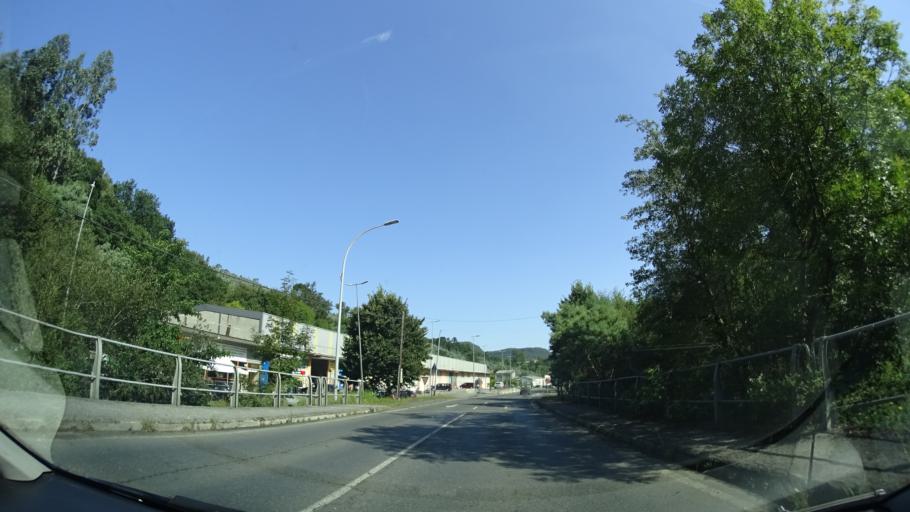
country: ES
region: Basque Country
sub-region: Bizkaia
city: Bakio
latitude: 43.4091
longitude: -2.8145
